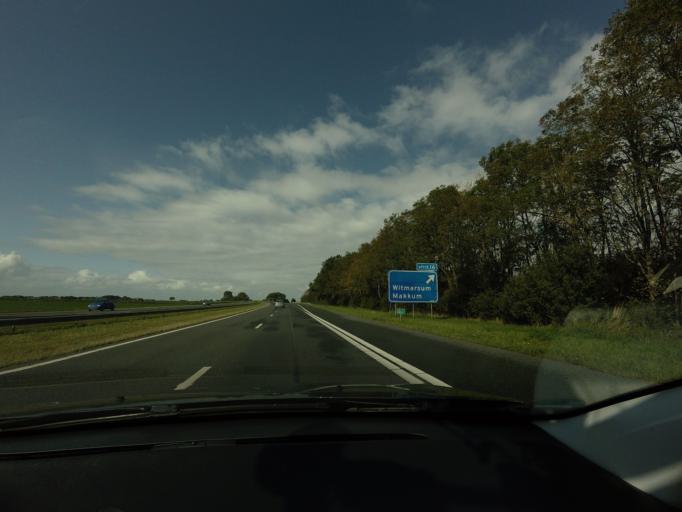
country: NL
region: Friesland
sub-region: Sudwest Fryslan
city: Makkum
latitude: 53.0866
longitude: 5.4545
